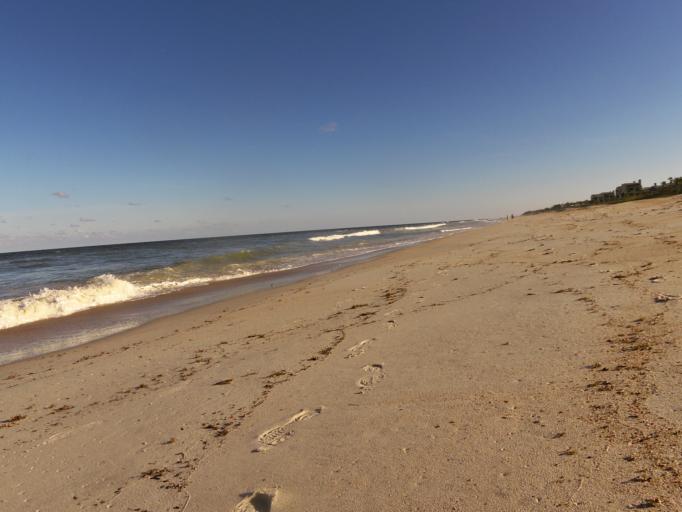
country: US
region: Florida
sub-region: Saint Johns County
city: Sawgrass
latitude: 30.1982
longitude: -81.3652
